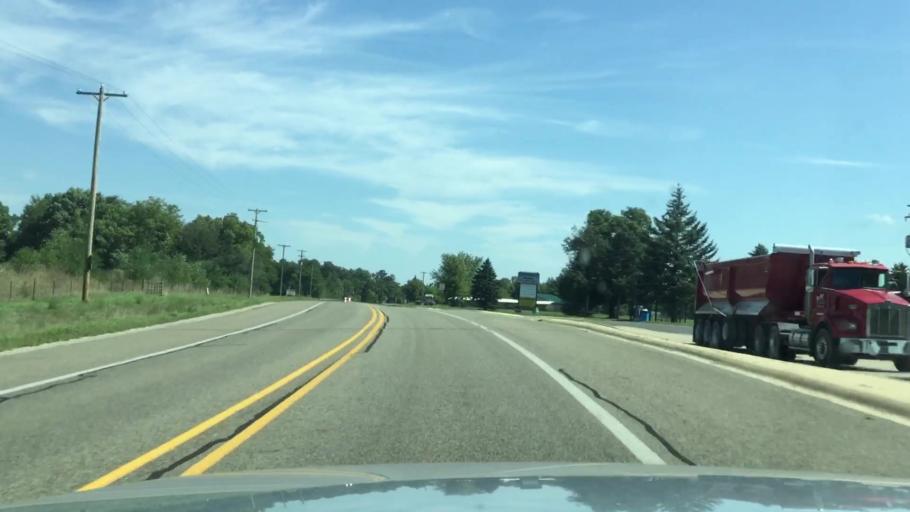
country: US
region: Michigan
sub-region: Jackson County
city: Brooklyn
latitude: 42.0491
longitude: -84.2731
